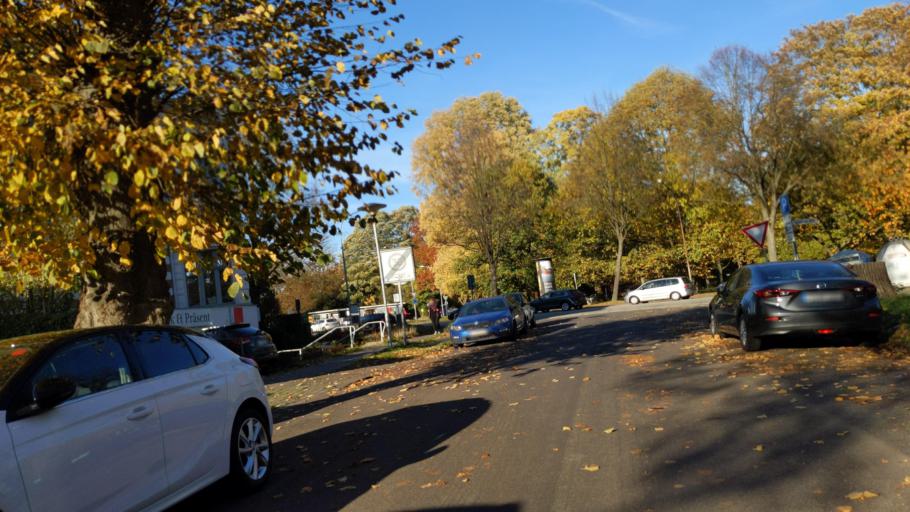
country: DE
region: Schleswig-Holstein
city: Luebeck
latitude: 53.8576
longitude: 10.6924
